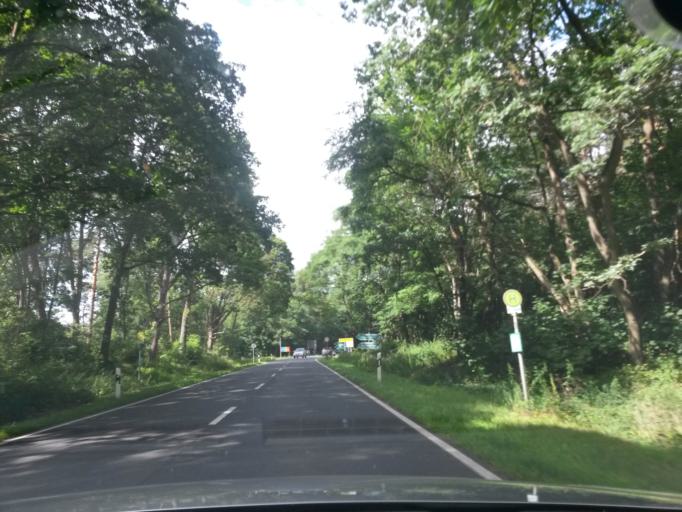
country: DE
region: Brandenburg
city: Chorin
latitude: 52.8992
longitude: 13.8893
